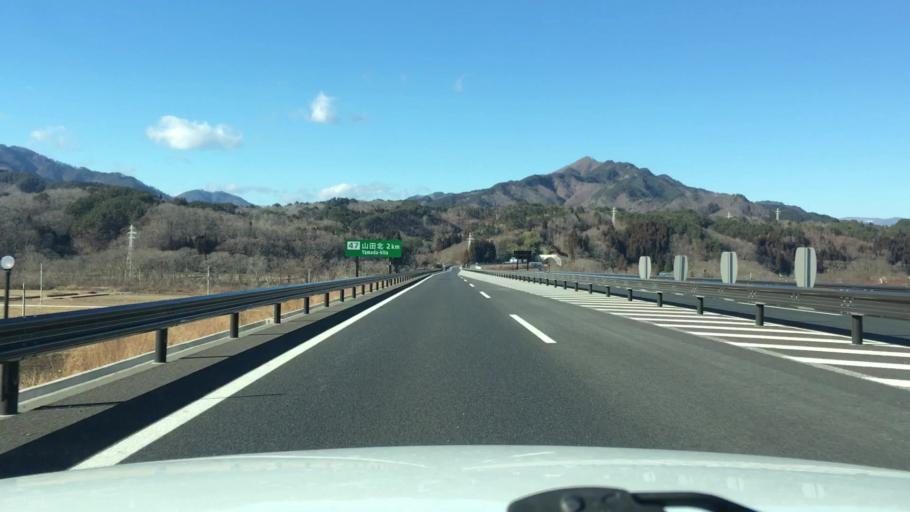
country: JP
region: Iwate
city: Yamada
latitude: 39.5234
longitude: 141.9287
